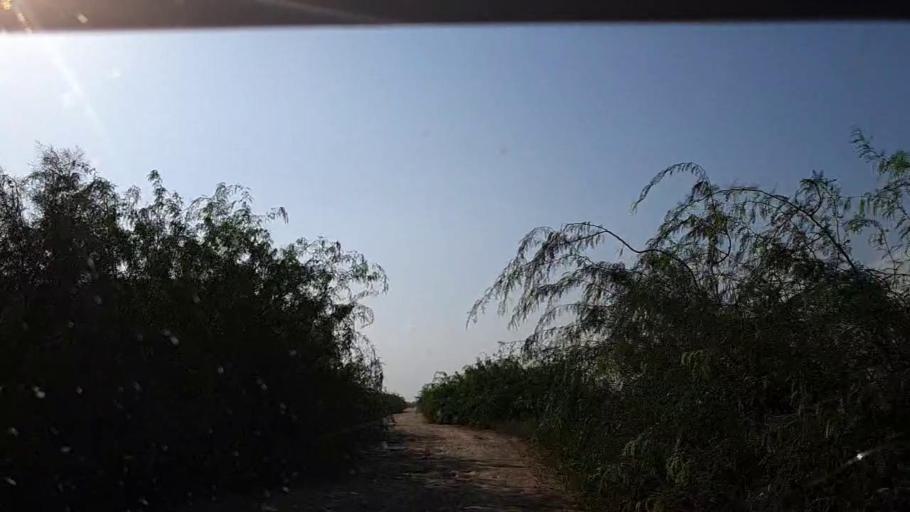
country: PK
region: Sindh
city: Adilpur
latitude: 27.9036
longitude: 69.2268
